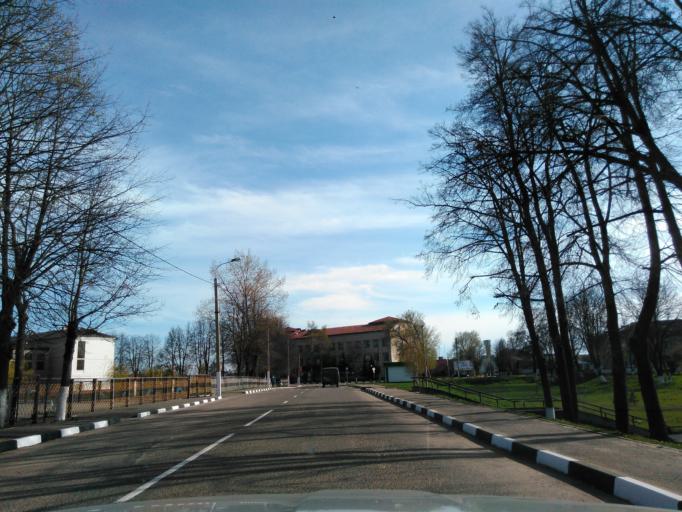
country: BY
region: Vitebsk
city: Chashniki
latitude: 54.8610
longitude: 29.1637
